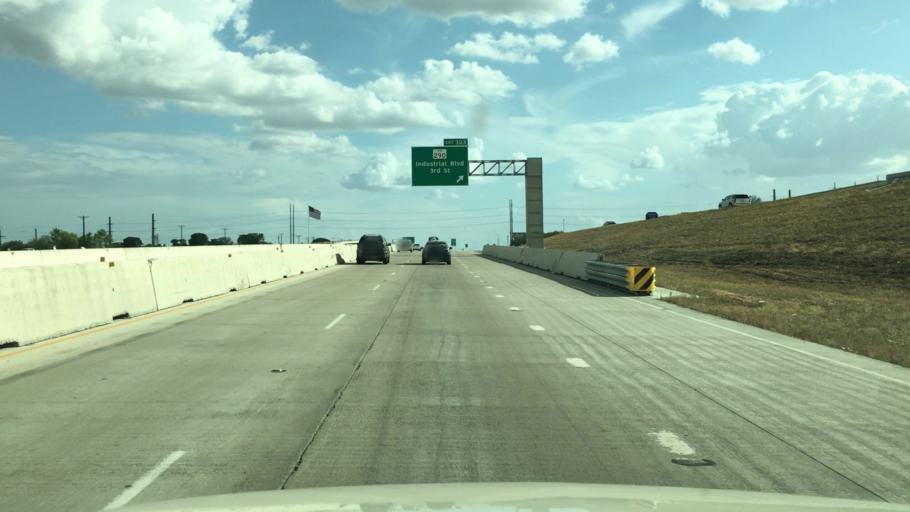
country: US
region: Texas
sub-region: Bell County
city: Temple
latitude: 31.1369
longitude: -97.3309
